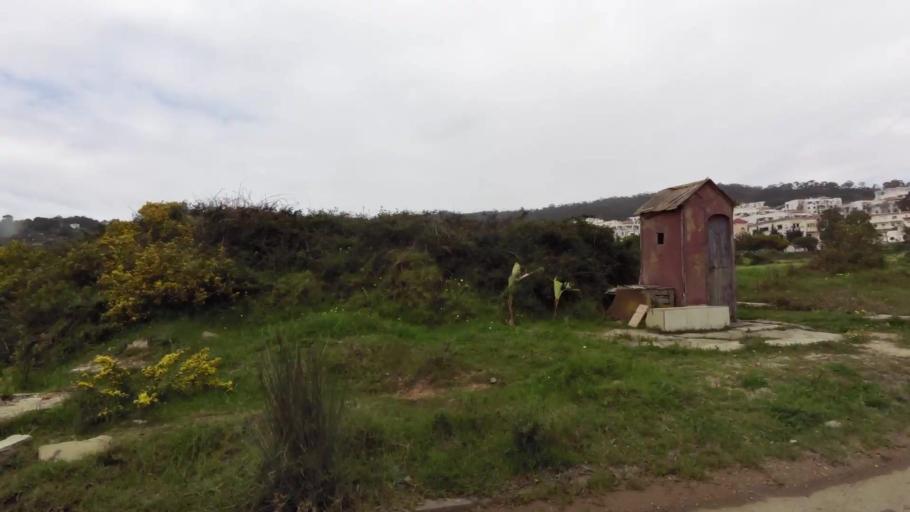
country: MA
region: Tanger-Tetouan
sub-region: Tanger-Assilah
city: Boukhalef
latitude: 35.7796
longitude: -5.8624
